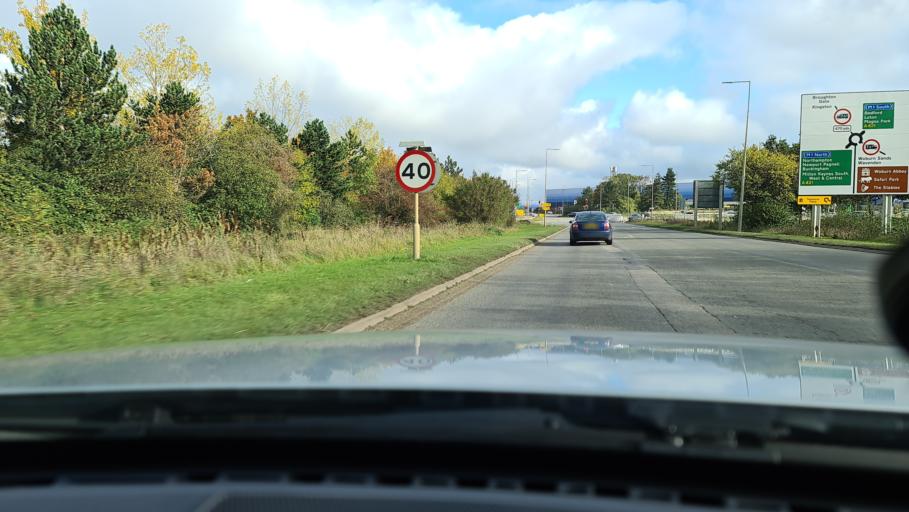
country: GB
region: England
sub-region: Milton Keynes
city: Wavendon
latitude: 52.0312
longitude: -0.6804
